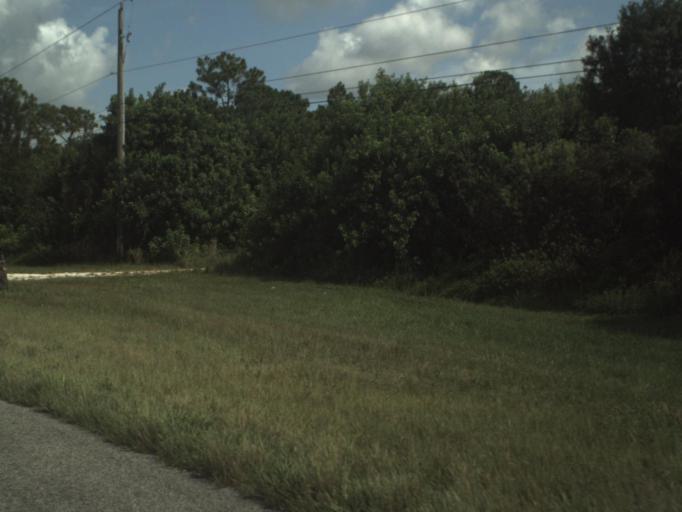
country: US
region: Florida
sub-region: Palm Beach County
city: Palm Beach Gardens
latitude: 26.8318
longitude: -80.1849
